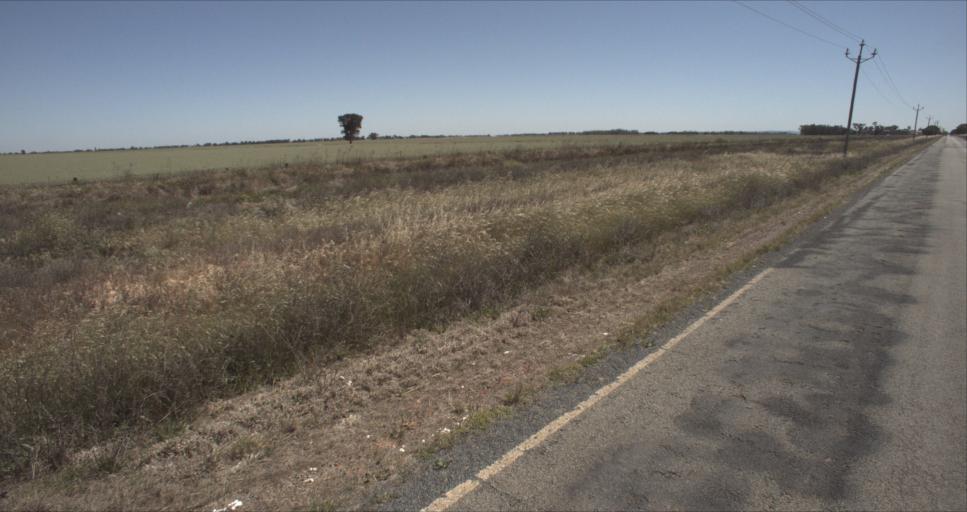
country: AU
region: New South Wales
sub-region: Leeton
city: Leeton
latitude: -34.5100
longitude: 146.2853
